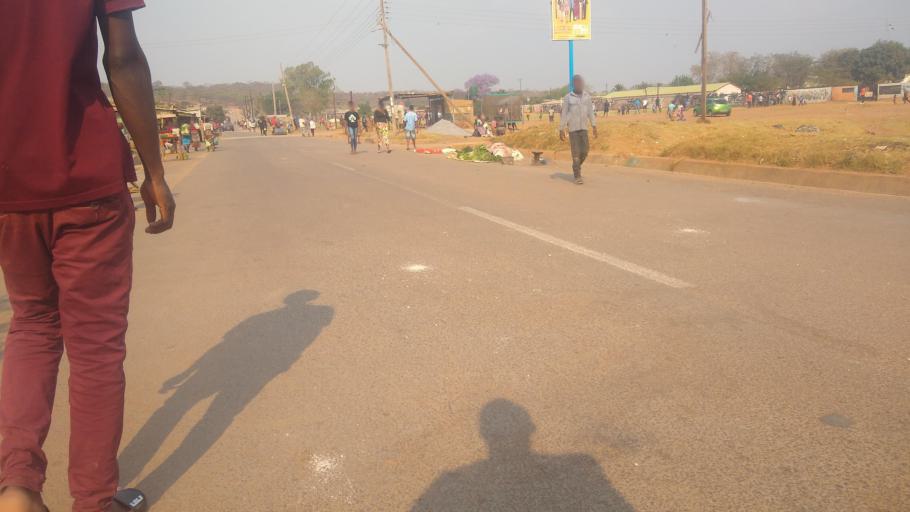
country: ZM
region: Lusaka
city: Lusaka
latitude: -15.4468
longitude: 28.3828
